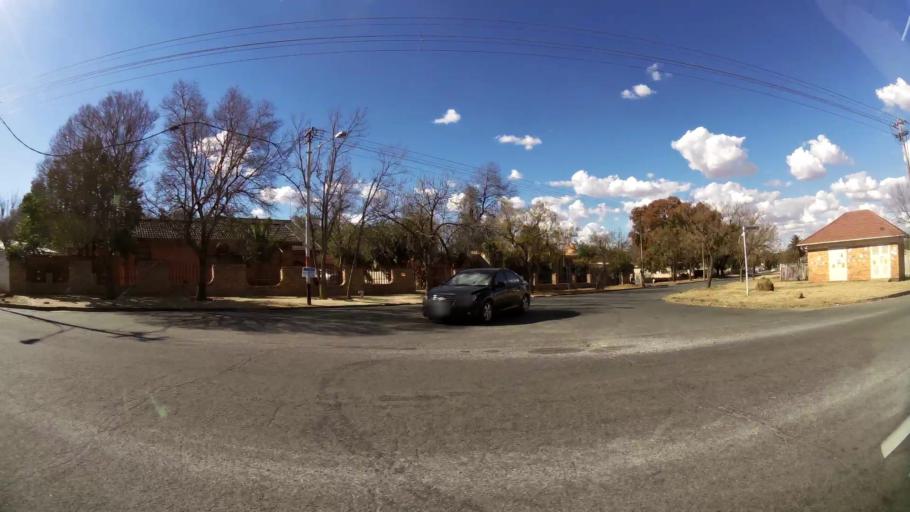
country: ZA
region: North-West
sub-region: Dr Kenneth Kaunda District Municipality
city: Klerksdorp
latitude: -26.8629
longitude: 26.6492
